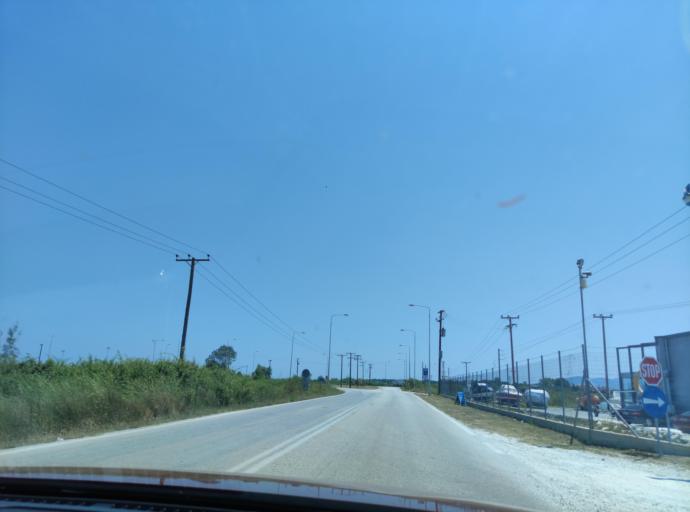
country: GR
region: East Macedonia and Thrace
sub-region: Nomos Kavalas
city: Keramoti
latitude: 40.8698
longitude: 24.7034
